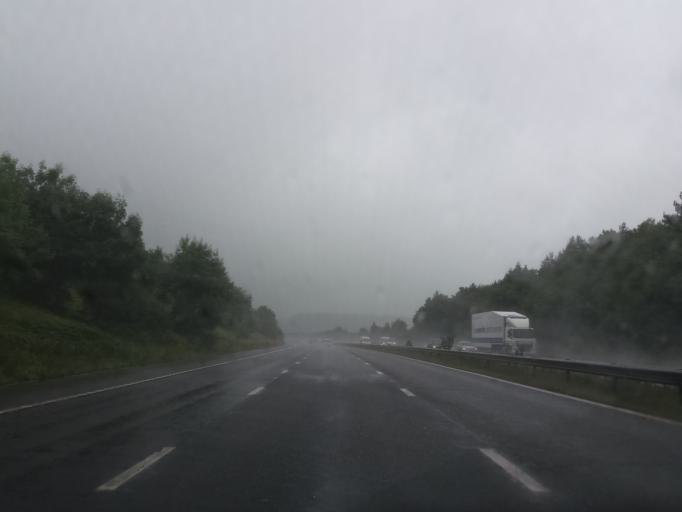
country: GB
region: England
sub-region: Leicestershire
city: Shepshed
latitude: 52.7383
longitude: -1.2807
